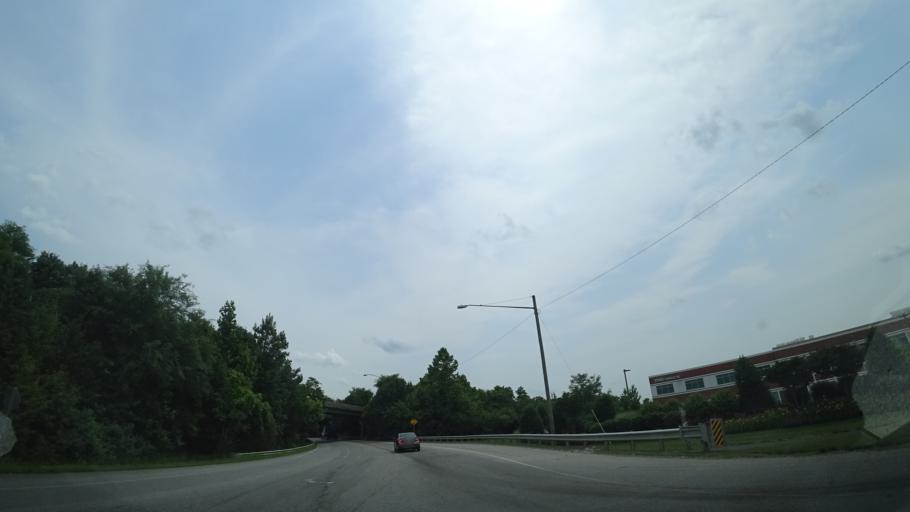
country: US
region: Virginia
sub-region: Prince William County
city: Woodbridge
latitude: 38.6755
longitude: -77.2404
